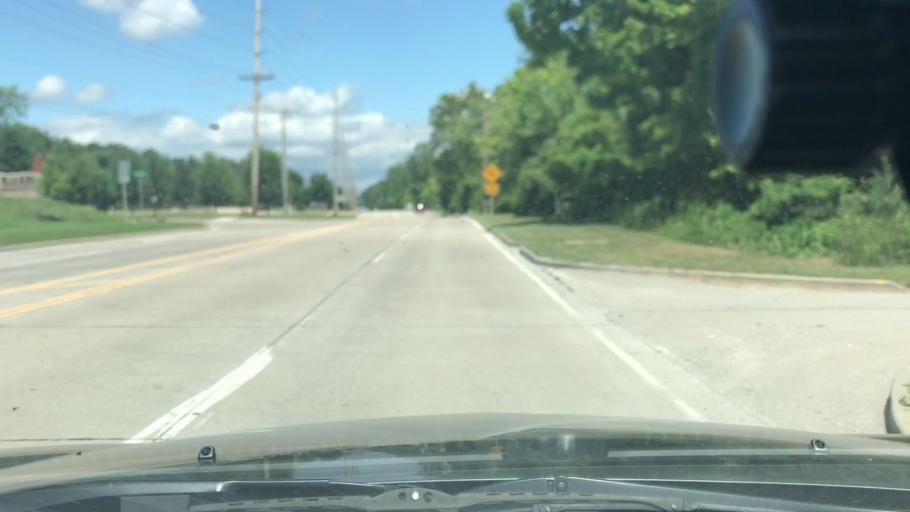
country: US
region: Missouri
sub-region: Saint Charles County
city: Saint Charles
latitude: 38.7555
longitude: -90.5007
